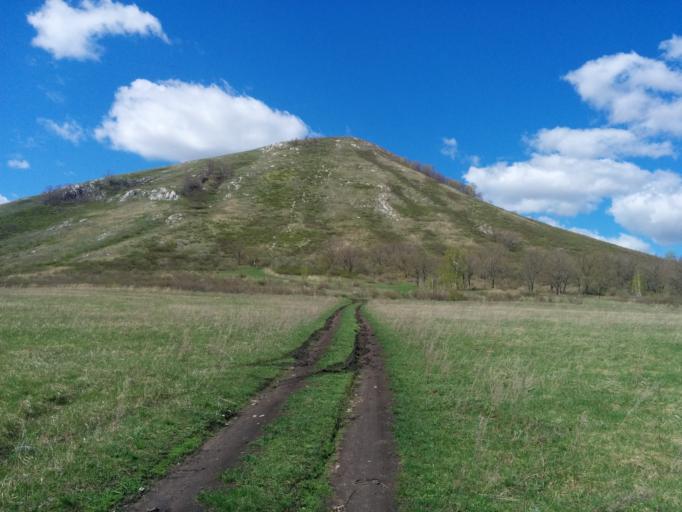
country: RU
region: Bashkortostan
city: Sterlitamak
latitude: 53.7420
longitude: 56.1059
